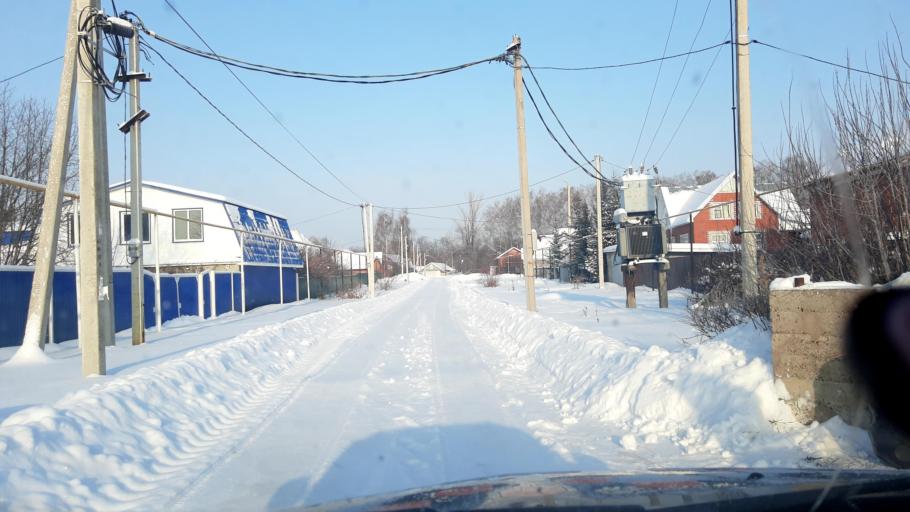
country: RU
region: Bashkortostan
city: Ufa
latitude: 54.5445
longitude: 55.9348
